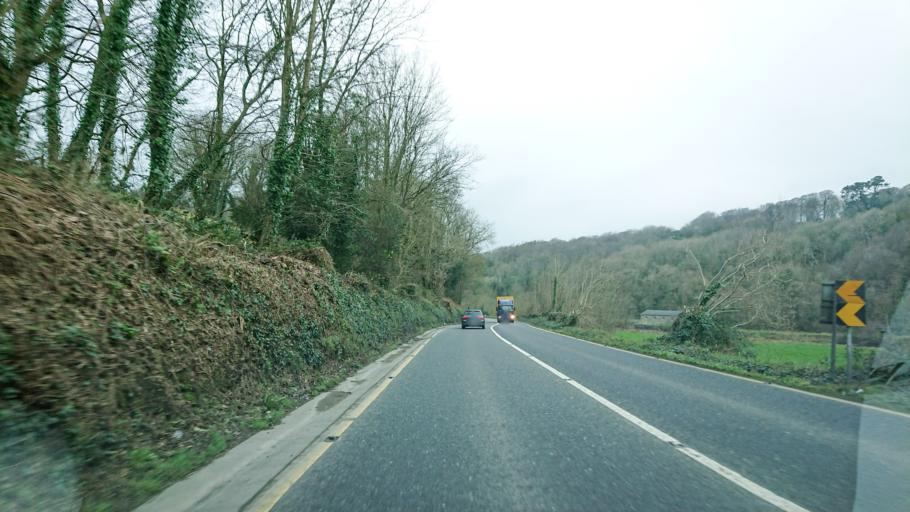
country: IE
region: Munster
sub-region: County Cork
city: Bandon
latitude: 51.7671
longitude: -8.6720
